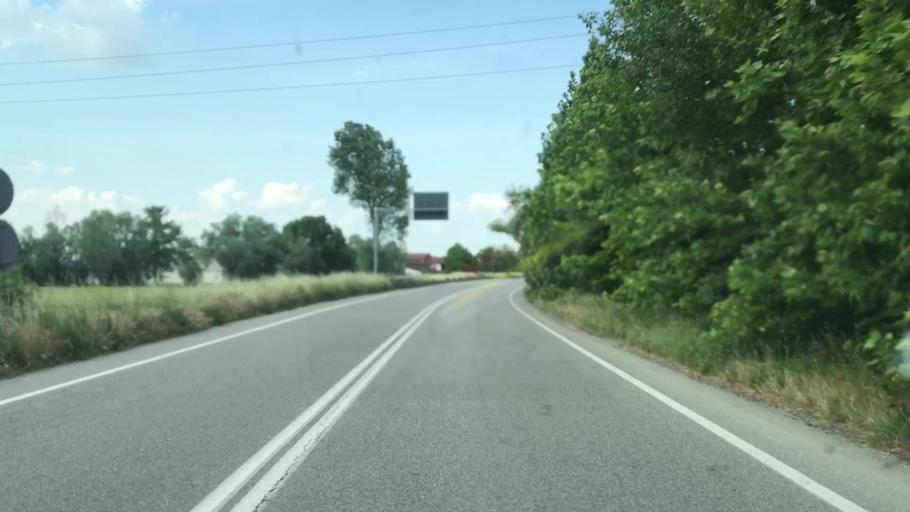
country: IT
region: Lombardy
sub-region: Provincia di Mantova
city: Castel Goffredo
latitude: 45.2963
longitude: 10.4907
